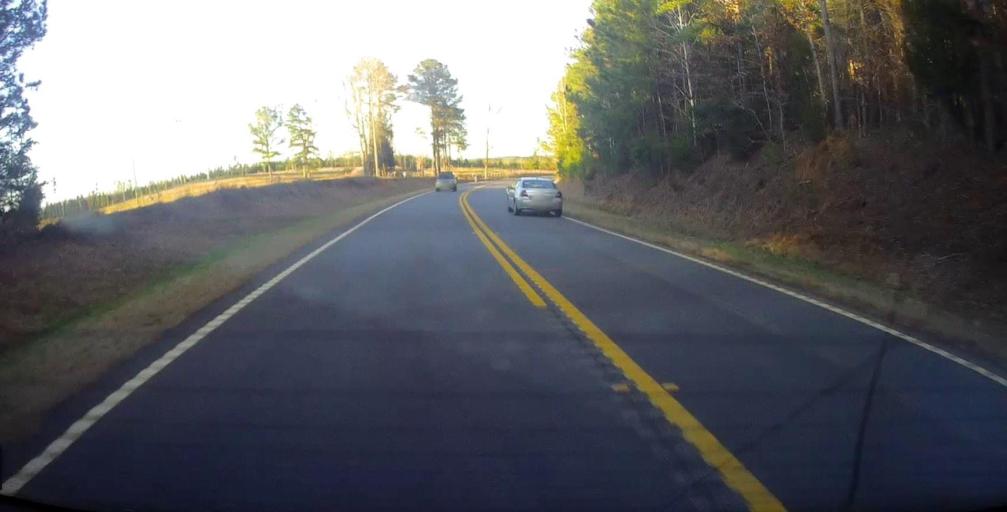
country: US
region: Georgia
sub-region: Talbot County
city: Sardis
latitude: 32.7040
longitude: -84.6987
